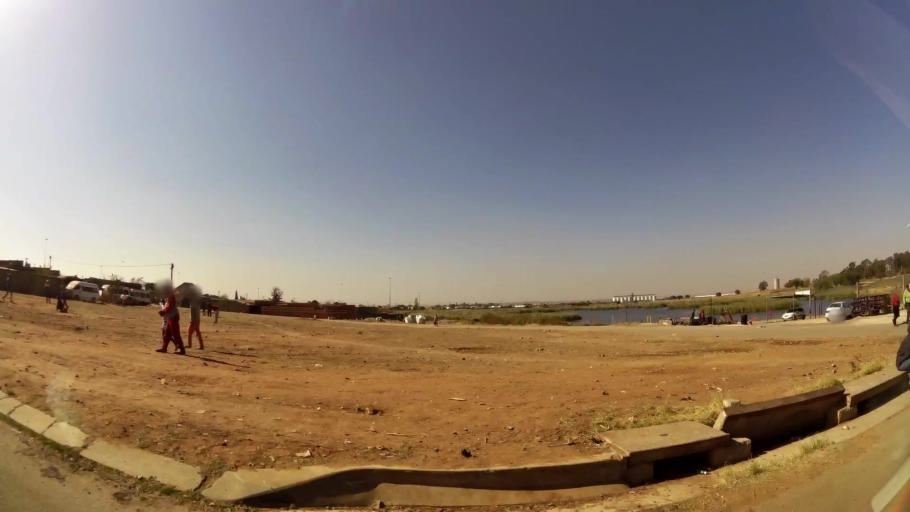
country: ZA
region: Gauteng
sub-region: Ekurhuleni Metropolitan Municipality
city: Tembisa
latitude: -26.0274
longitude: 28.2387
